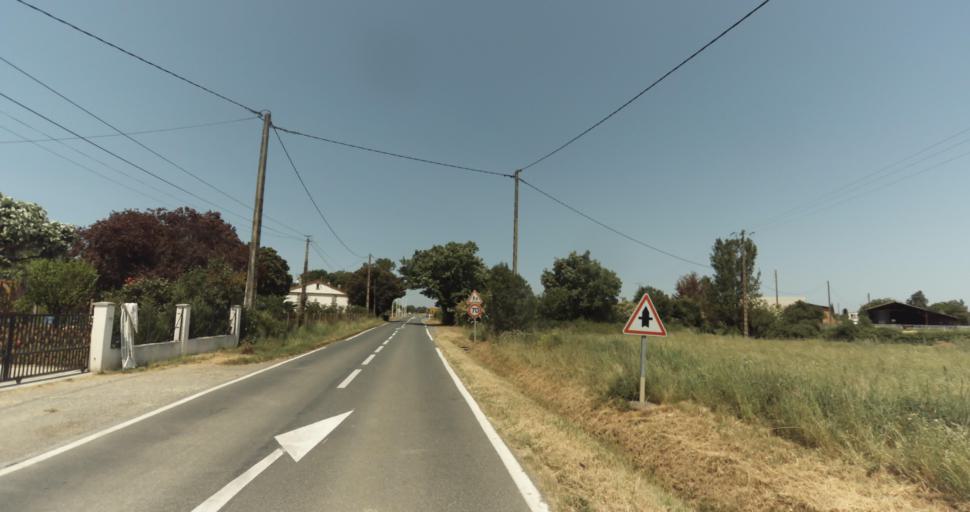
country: FR
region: Midi-Pyrenees
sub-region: Departement de la Haute-Garonne
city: Leguevin
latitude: 43.5905
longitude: 1.2522
